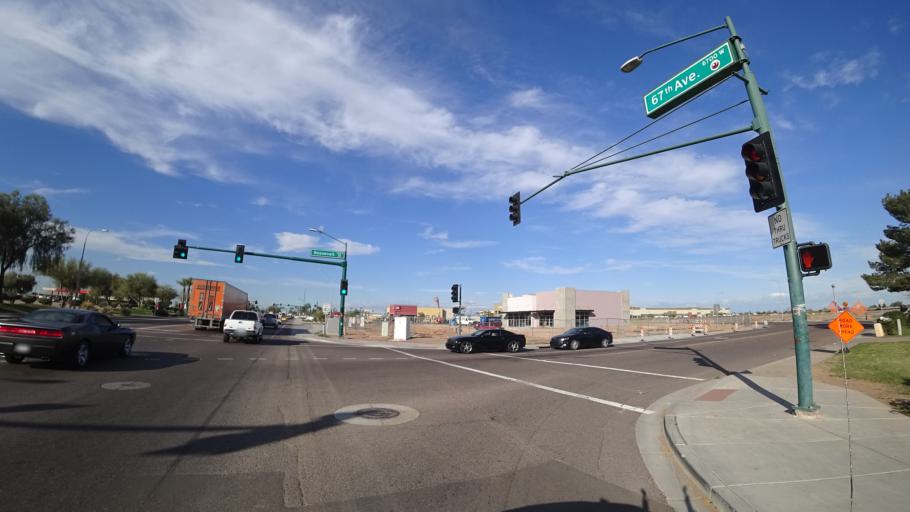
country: US
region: Arizona
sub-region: Maricopa County
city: Tolleson
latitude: 33.4586
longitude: -112.2033
